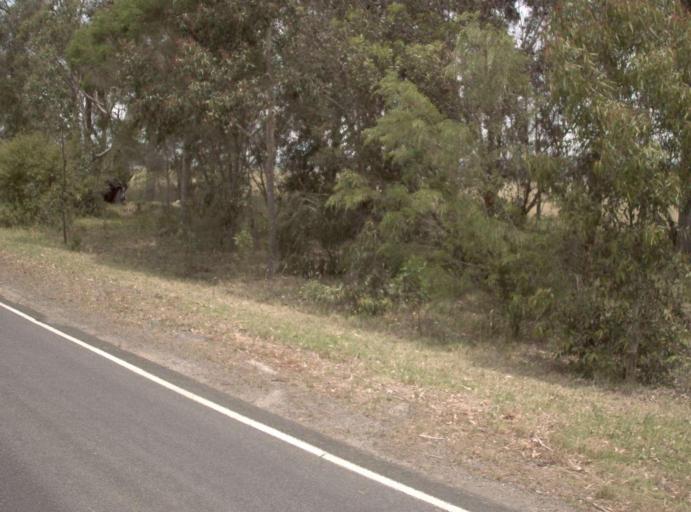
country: AU
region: Victoria
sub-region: Latrobe
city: Traralgon
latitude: -38.4672
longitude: 146.7182
